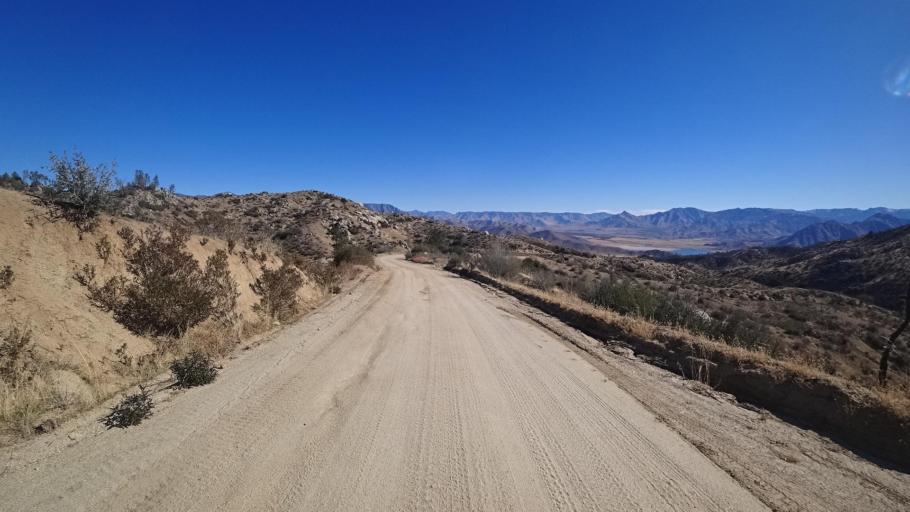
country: US
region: California
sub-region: Kern County
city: Wofford Heights
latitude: 35.7052
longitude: -118.4994
